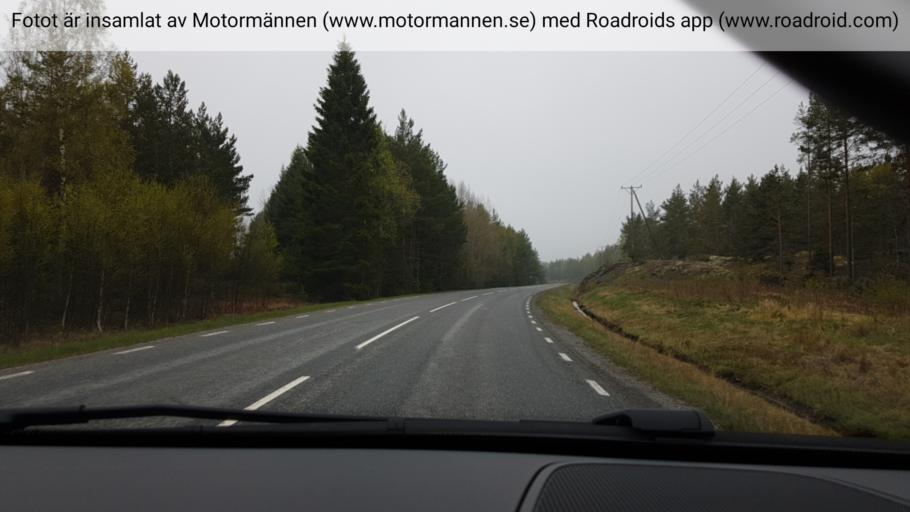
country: SE
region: Stockholm
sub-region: Nynashamns Kommun
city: Nynashamn
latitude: 58.9599
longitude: 17.9974
